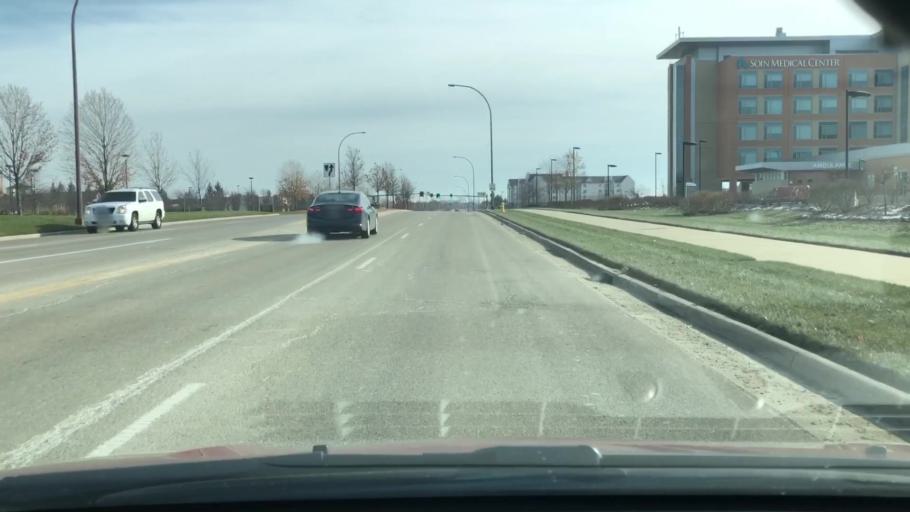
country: US
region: Ohio
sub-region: Greene County
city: Wright-Patterson AFB
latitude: 39.7722
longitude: -84.0639
